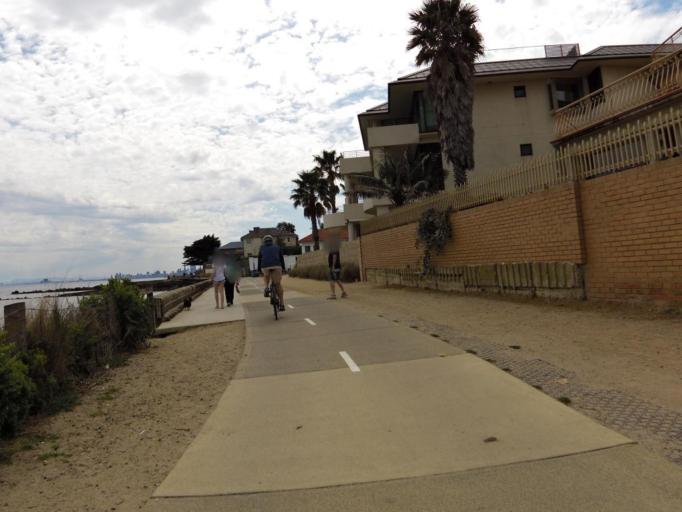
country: AU
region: Victoria
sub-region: Bayside
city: North Brighton
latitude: -37.9038
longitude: 144.9841
